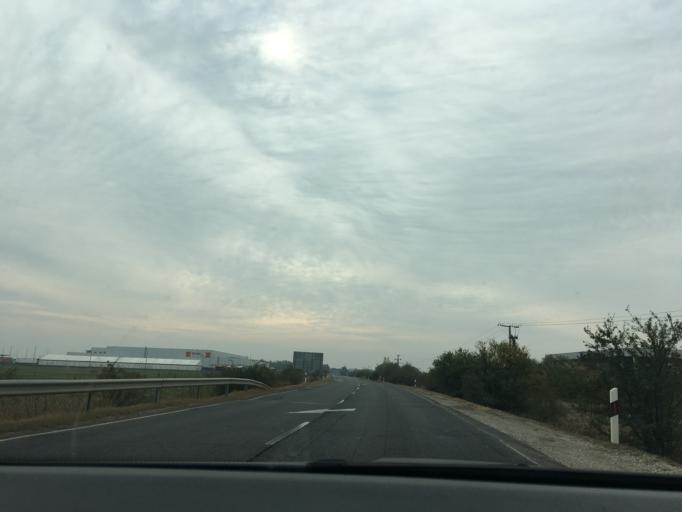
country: HU
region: Jasz-Nagykun-Szolnok
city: Karcag
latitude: 47.3048
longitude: 20.9362
